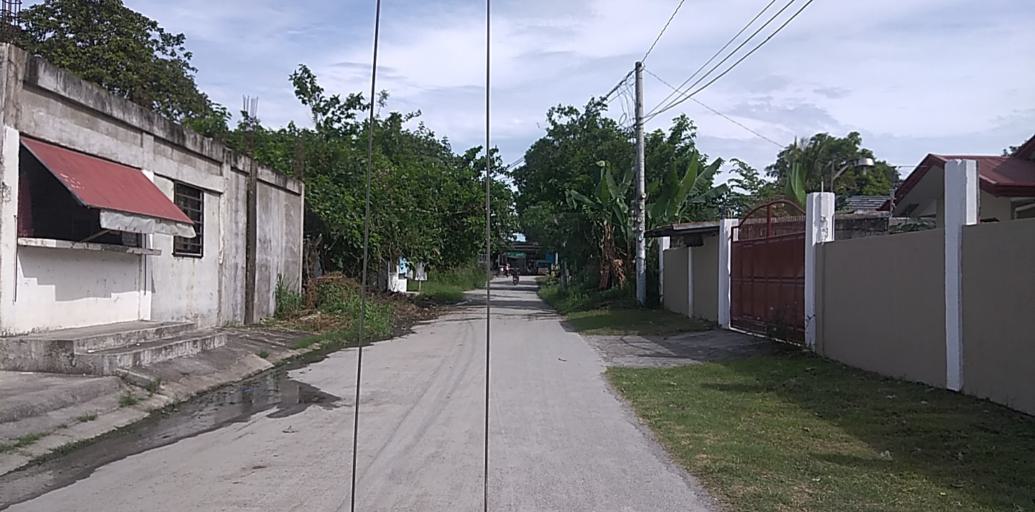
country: PH
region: Central Luzon
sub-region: Province of Pampanga
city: Angeles City
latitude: 15.1304
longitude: 120.5601
